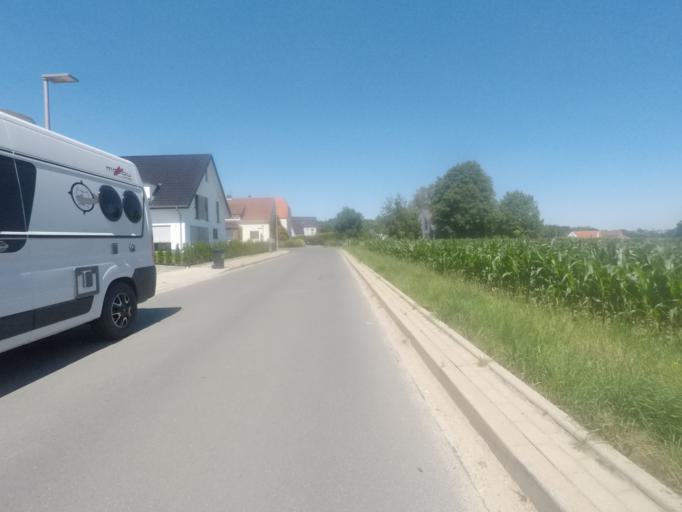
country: DE
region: North Rhine-Westphalia
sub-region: Regierungsbezirk Detmold
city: Bielefeld
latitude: 52.0804
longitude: 8.5199
